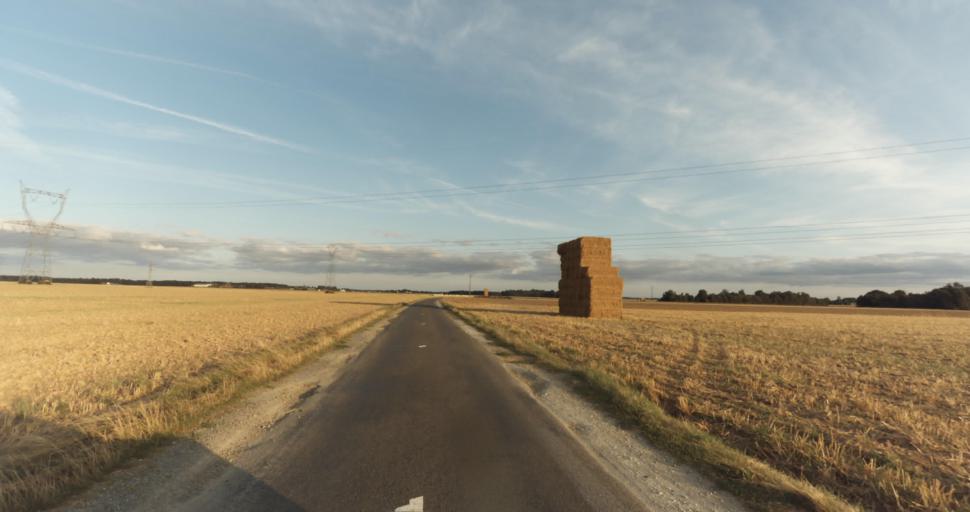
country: FR
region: Haute-Normandie
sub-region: Departement de l'Eure
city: Saint-Germain-sur-Avre
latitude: 48.8556
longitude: 1.2570
